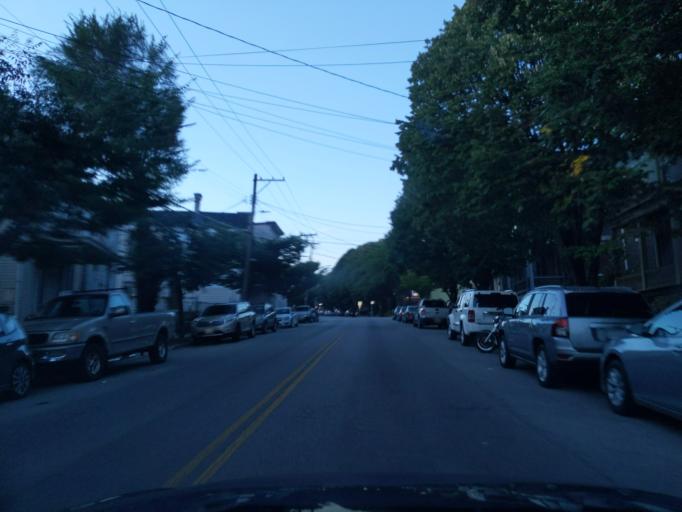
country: US
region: Kentucky
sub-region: Campbell County
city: Newport
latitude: 39.1228
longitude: -84.5202
